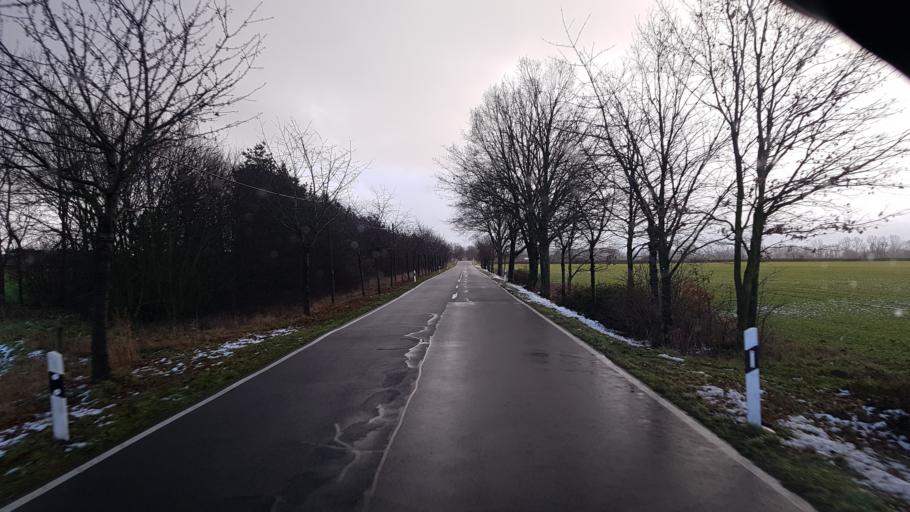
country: DE
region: Brandenburg
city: Heinersbruck
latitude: 51.8325
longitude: 14.5050
